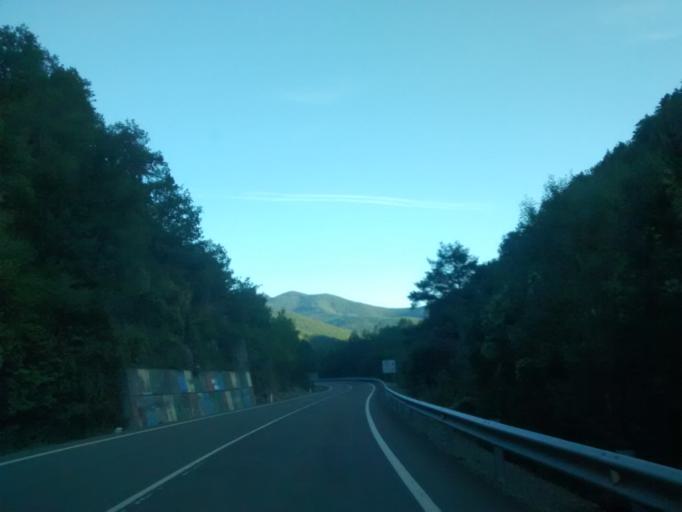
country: ES
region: Aragon
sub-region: Provincia de Huesca
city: Aragues del Puerto
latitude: 42.6966
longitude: -0.7427
